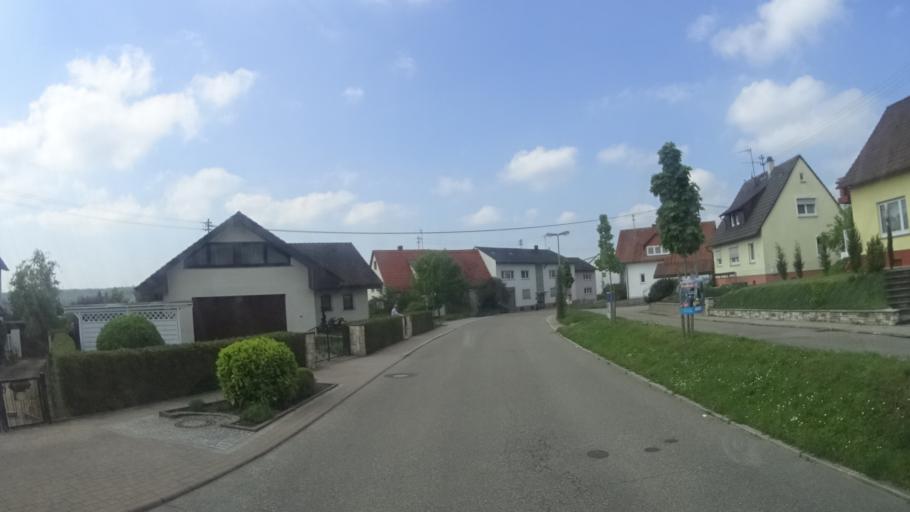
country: DE
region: Baden-Wuerttemberg
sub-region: Karlsruhe Region
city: Zaisenhausen
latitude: 49.1899
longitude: 8.8157
